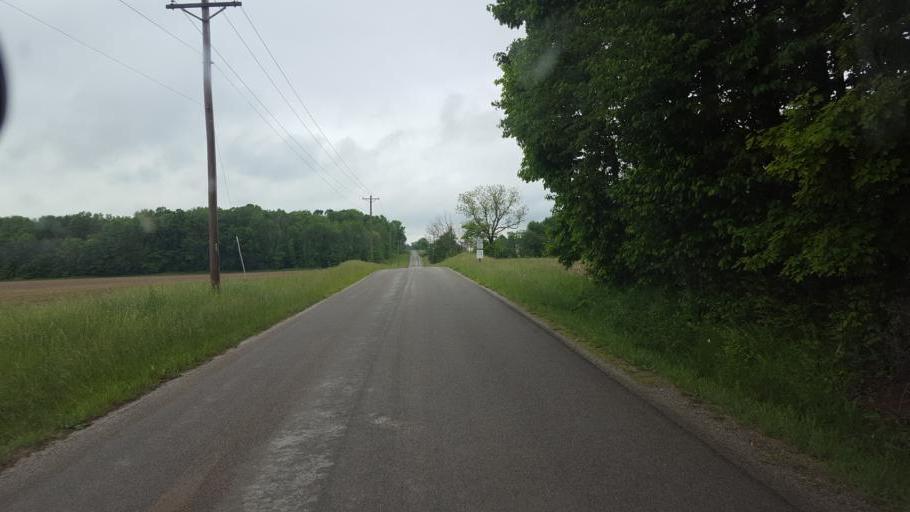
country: US
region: Ohio
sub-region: Morrow County
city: Mount Gilead
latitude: 40.4743
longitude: -82.7571
